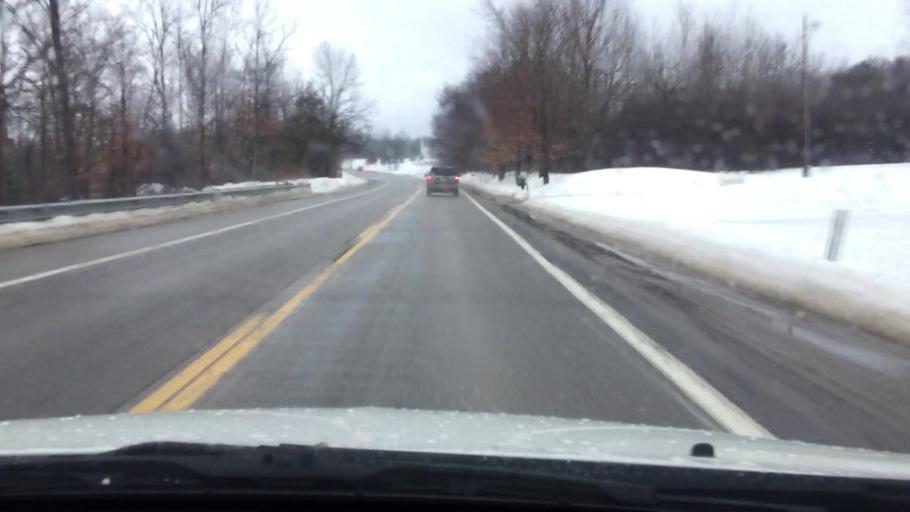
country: US
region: Michigan
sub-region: Charlevoix County
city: East Jordan
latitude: 45.1993
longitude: -85.1652
